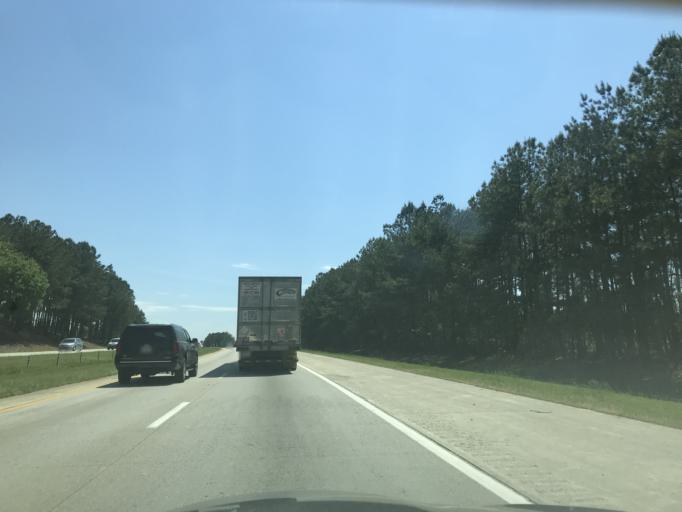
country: US
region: North Carolina
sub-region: Wake County
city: Garner
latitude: 35.6157
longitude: -78.5675
